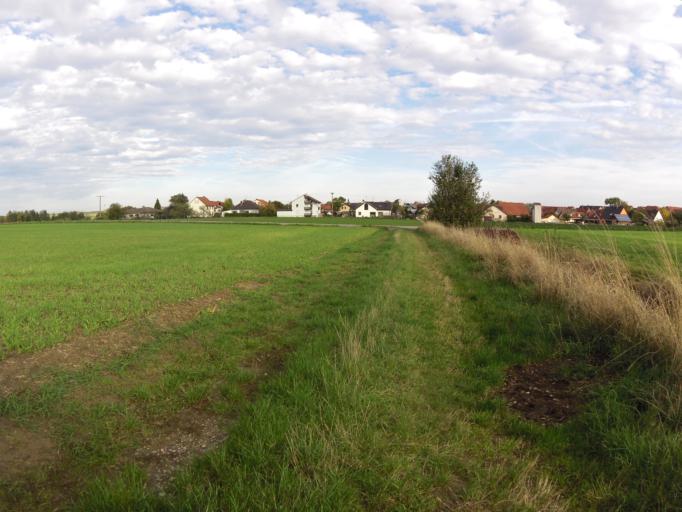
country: DE
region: Bavaria
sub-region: Regierungsbezirk Unterfranken
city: Biebelried
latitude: 49.7306
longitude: 10.0829
